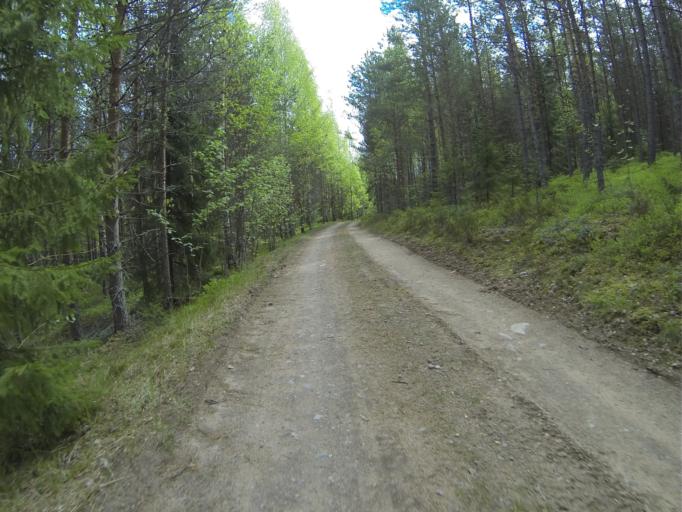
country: FI
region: Varsinais-Suomi
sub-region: Salo
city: Halikko
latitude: 60.3193
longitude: 23.0802
